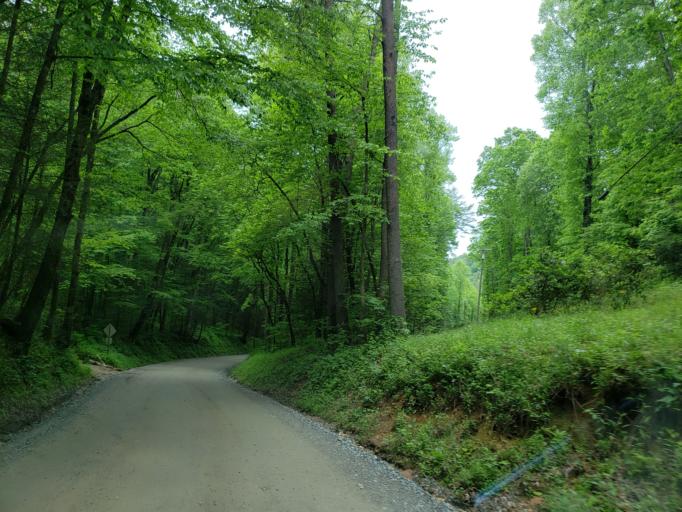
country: US
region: Georgia
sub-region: Fannin County
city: Blue Ridge
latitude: 34.8502
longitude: -84.4177
